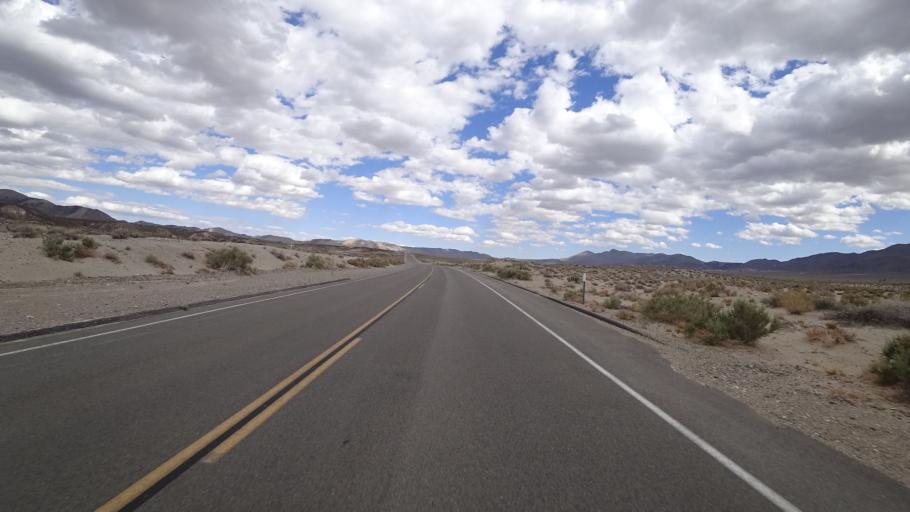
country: US
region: California
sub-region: Inyo County
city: Lone Pine
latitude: 36.3491
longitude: -117.7716
